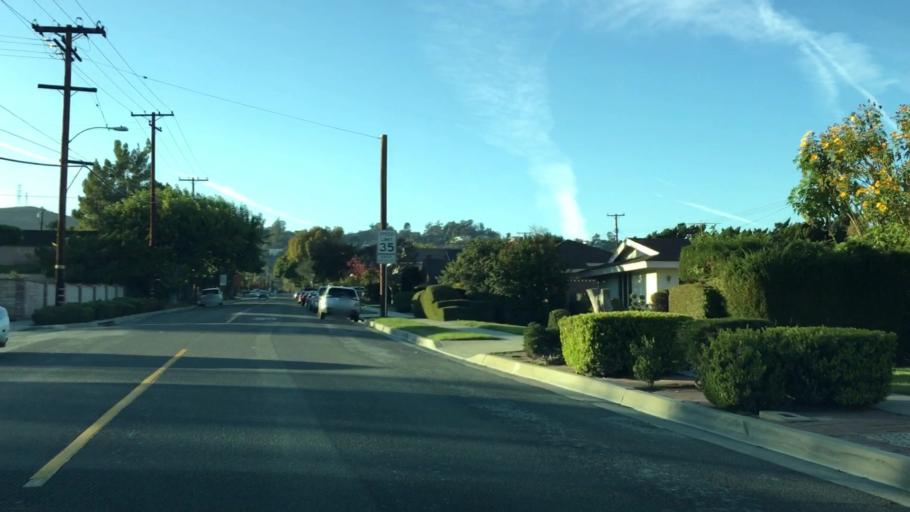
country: US
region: California
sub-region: Los Angeles County
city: Hacienda Heights
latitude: 33.9888
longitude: -117.9801
